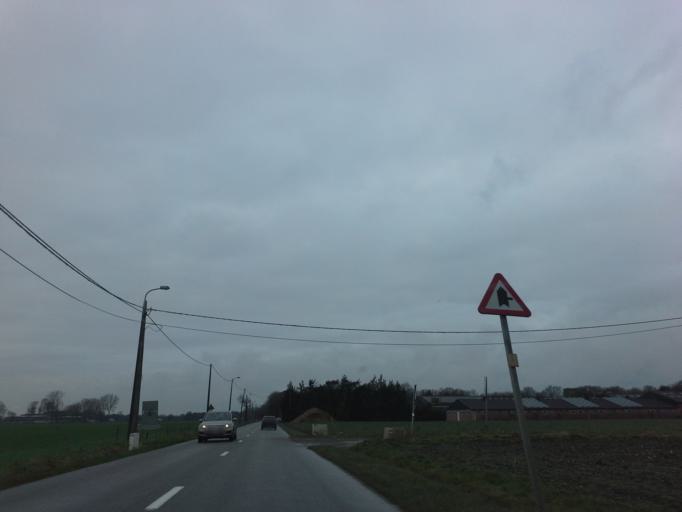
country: BE
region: Flanders
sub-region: Provincie Limburg
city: Leopoldsburg
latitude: 51.1557
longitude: 5.2327
